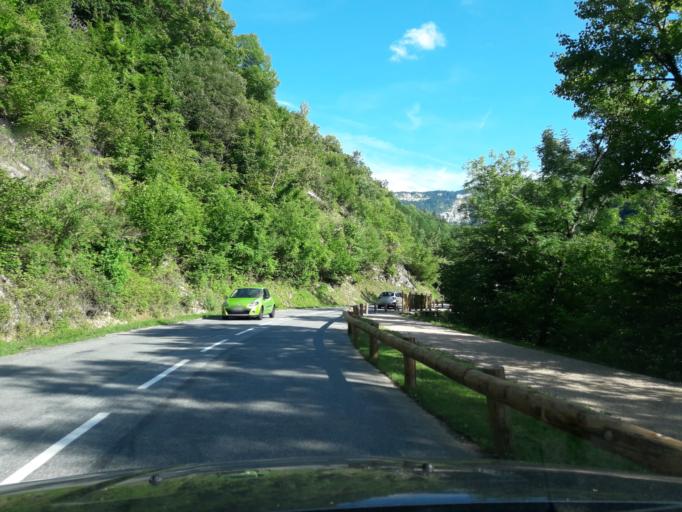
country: FR
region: Rhone-Alpes
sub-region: Departement de la Savoie
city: Novalaise
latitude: 45.5645
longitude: 5.8110
